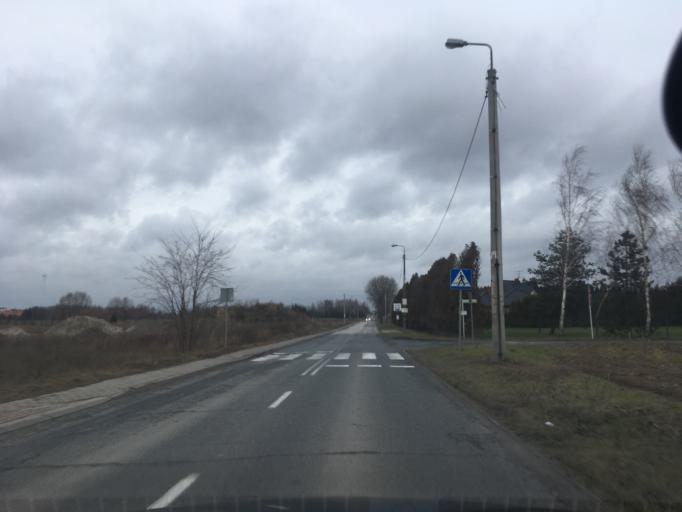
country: PL
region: Masovian Voivodeship
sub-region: Powiat piaseczynski
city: Lesznowola
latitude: 52.0956
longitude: 20.9337
